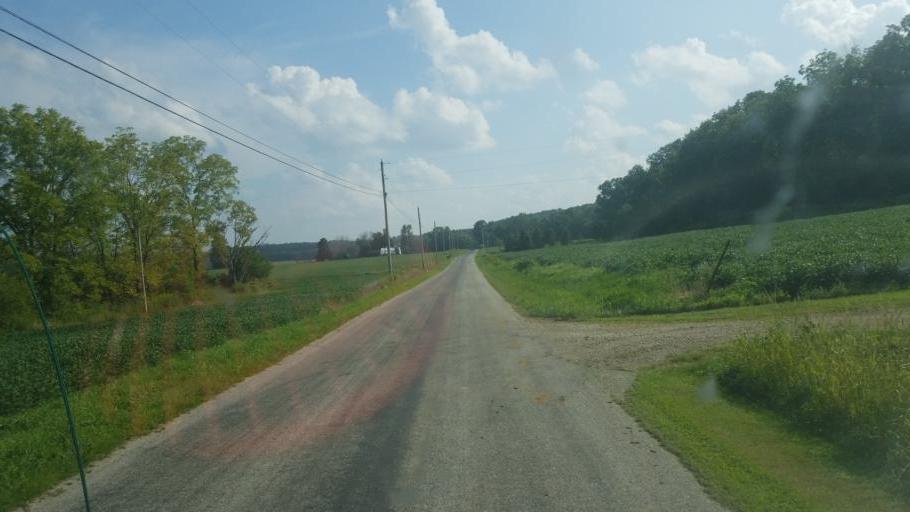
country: US
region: Ohio
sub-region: Medina County
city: Lodi
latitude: 40.9630
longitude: -82.0348
